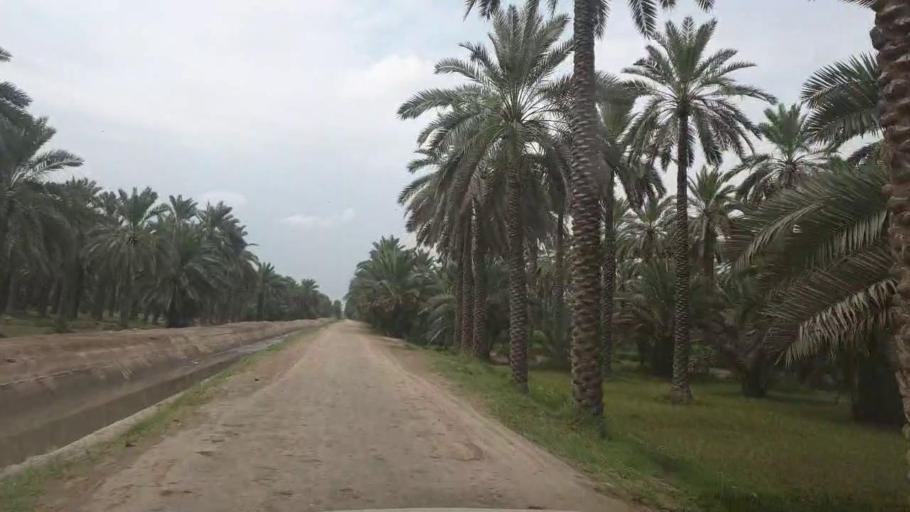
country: PK
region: Sindh
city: Sukkur
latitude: 27.6238
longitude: 68.8073
